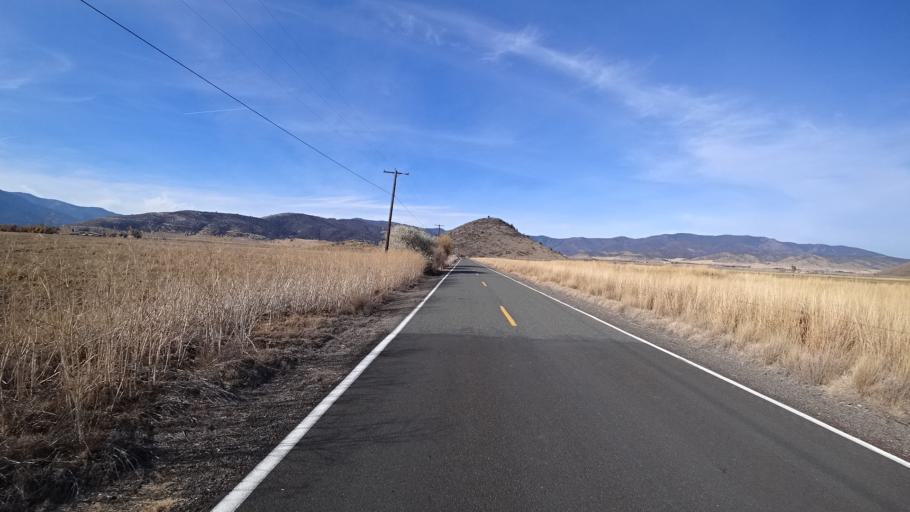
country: US
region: California
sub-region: Siskiyou County
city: Weed
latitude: 41.5342
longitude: -122.5126
